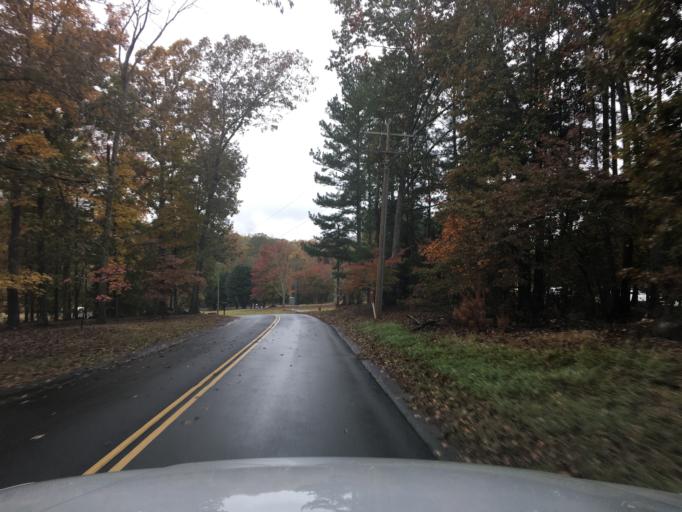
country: US
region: South Carolina
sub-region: Pickens County
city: Central
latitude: 34.7352
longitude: -82.7750
